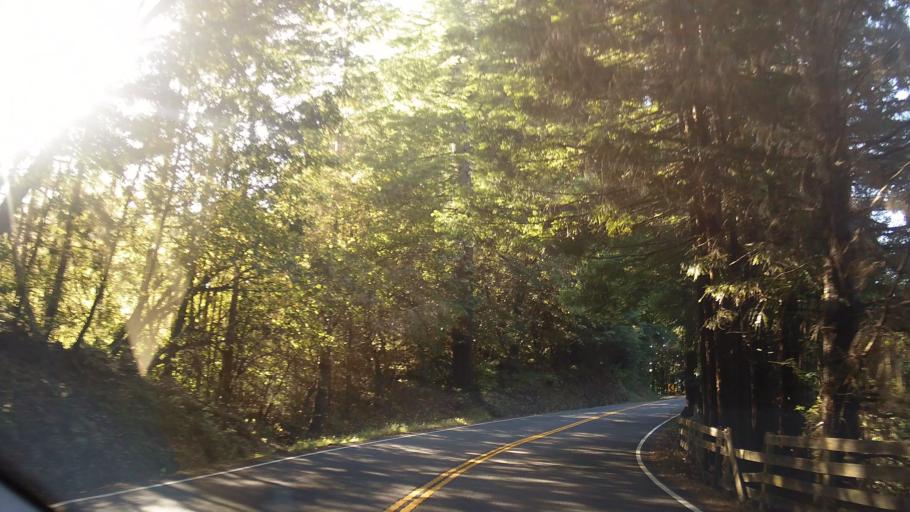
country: US
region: California
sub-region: Mendocino County
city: Fort Bragg
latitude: 39.3585
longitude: -123.6193
